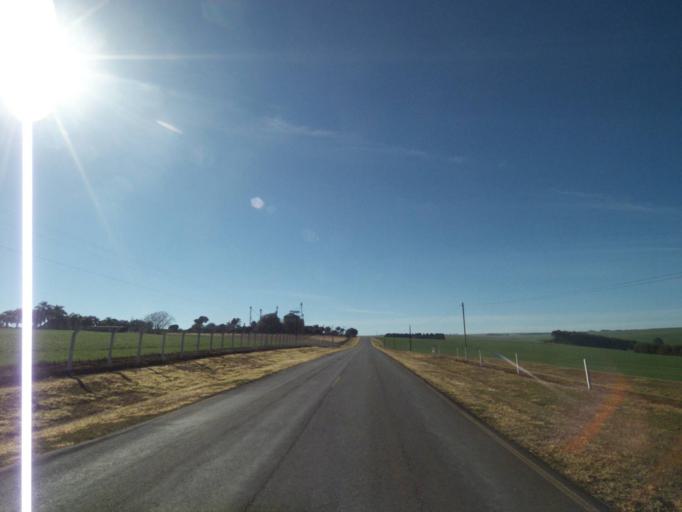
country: BR
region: Parana
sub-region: Tibagi
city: Tibagi
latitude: -24.5234
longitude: -50.3619
